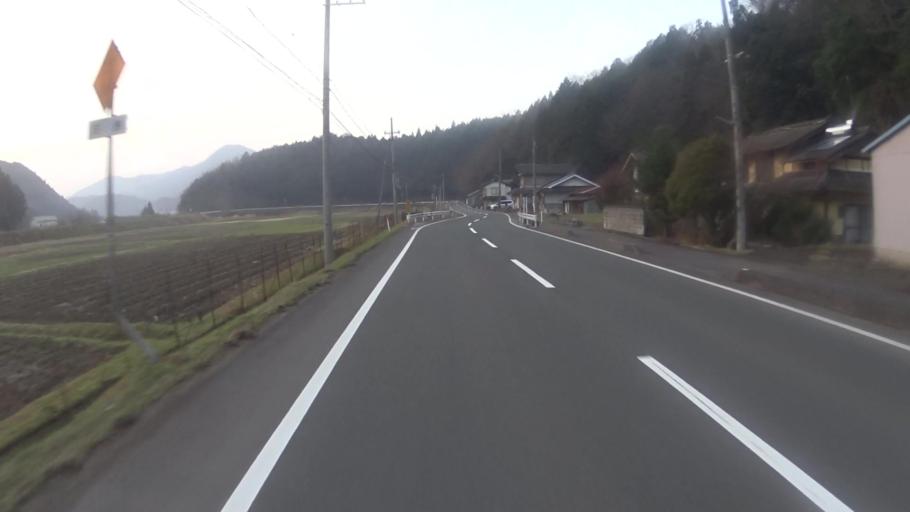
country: JP
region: Kyoto
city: Maizuru
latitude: 35.3676
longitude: 135.4306
